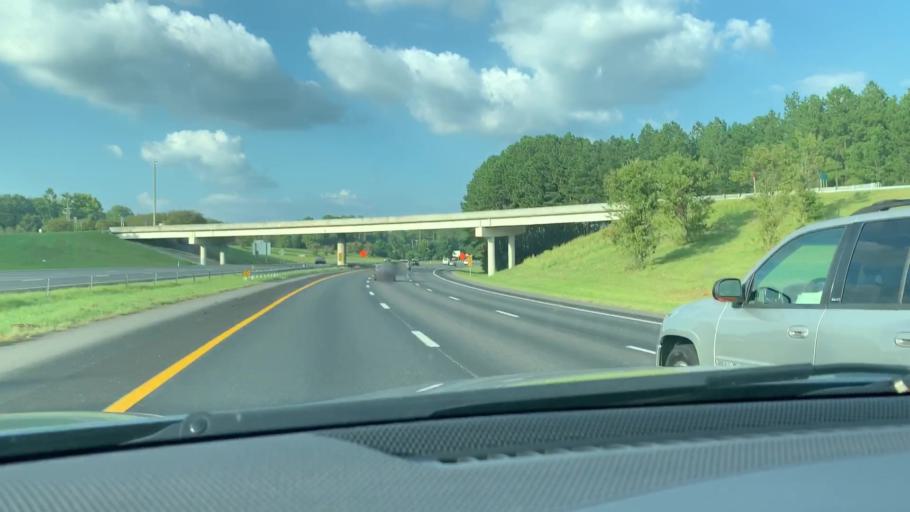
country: US
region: South Carolina
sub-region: Richland County
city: Woodfield
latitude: 34.0399
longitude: -80.9370
